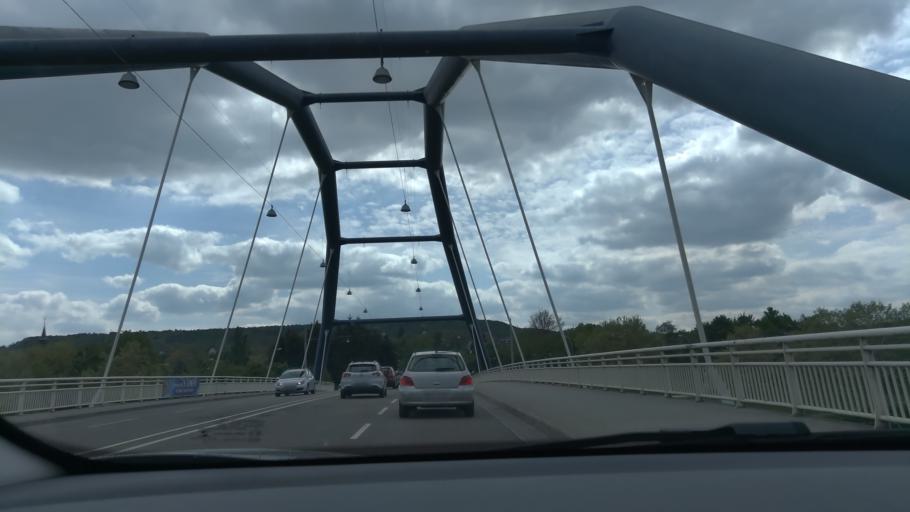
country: DE
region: Saarland
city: Saarbrucken
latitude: 49.2220
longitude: 7.0182
